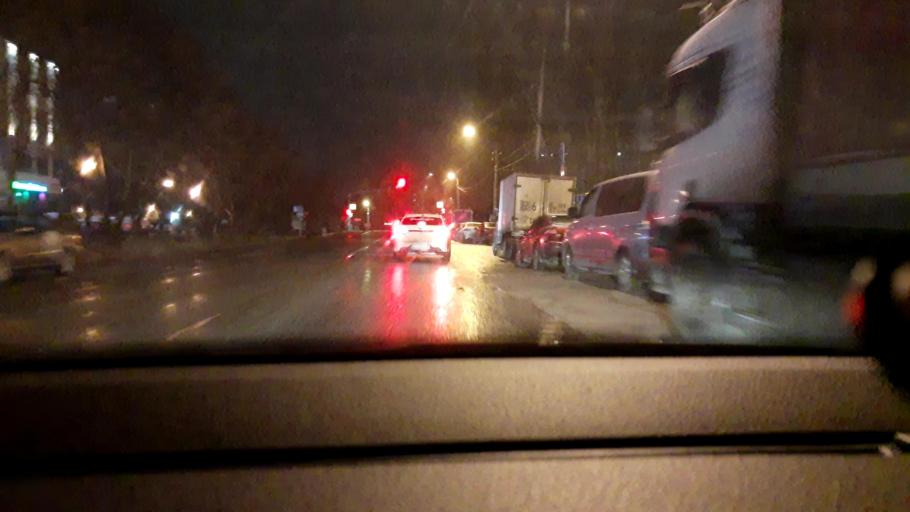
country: RU
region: Moskovskaya
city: Shchelkovo
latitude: 55.9382
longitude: 37.9741
